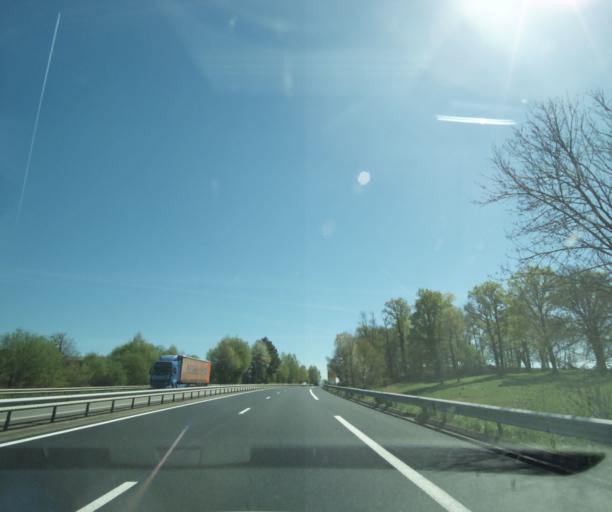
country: FR
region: Limousin
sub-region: Departement de la Haute-Vienne
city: Boisseuil
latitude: 45.7638
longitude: 1.3285
